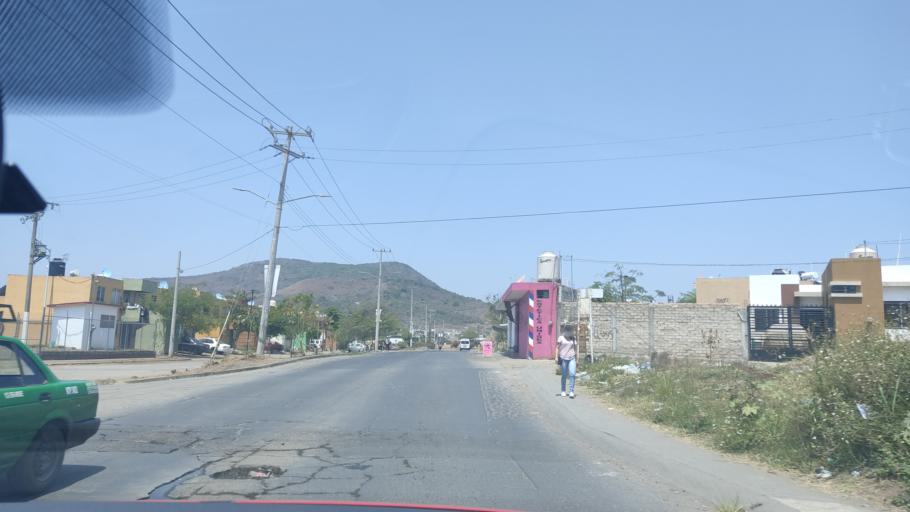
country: MX
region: Nayarit
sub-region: Tepic
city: La Corregidora
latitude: 21.4925
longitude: -104.8195
